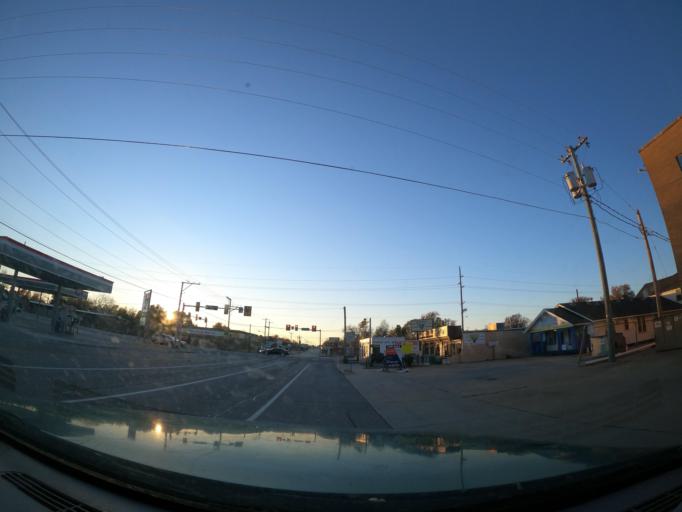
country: US
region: Oklahoma
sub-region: Tulsa County
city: Tulsa
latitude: 36.1407
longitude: -95.9398
